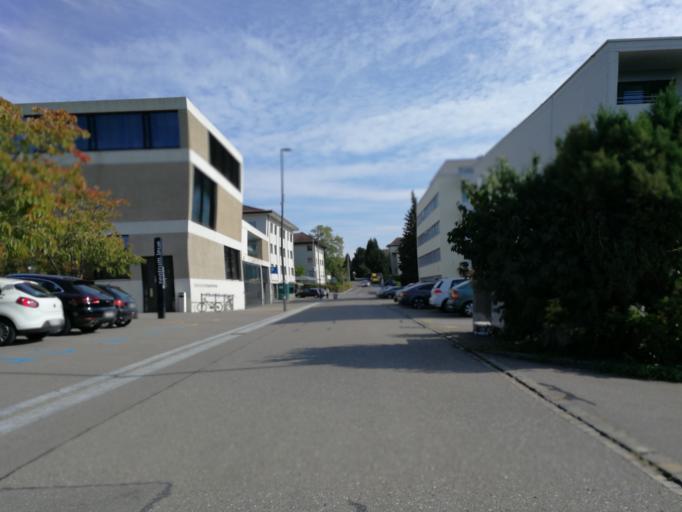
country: CH
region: Zurich
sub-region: Bezirk Meilen
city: Maennedorf / Dorfkern
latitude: 47.2530
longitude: 8.6946
